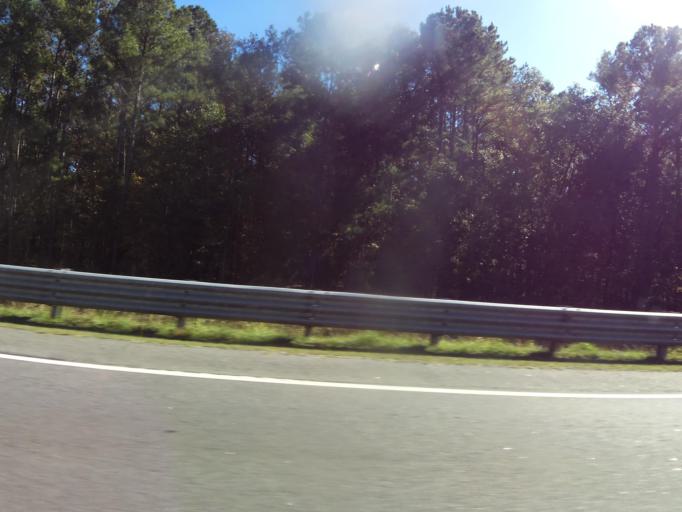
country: US
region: Georgia
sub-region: Bryan County
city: Richmond Hill
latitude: 31.9344
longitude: -81.3218
